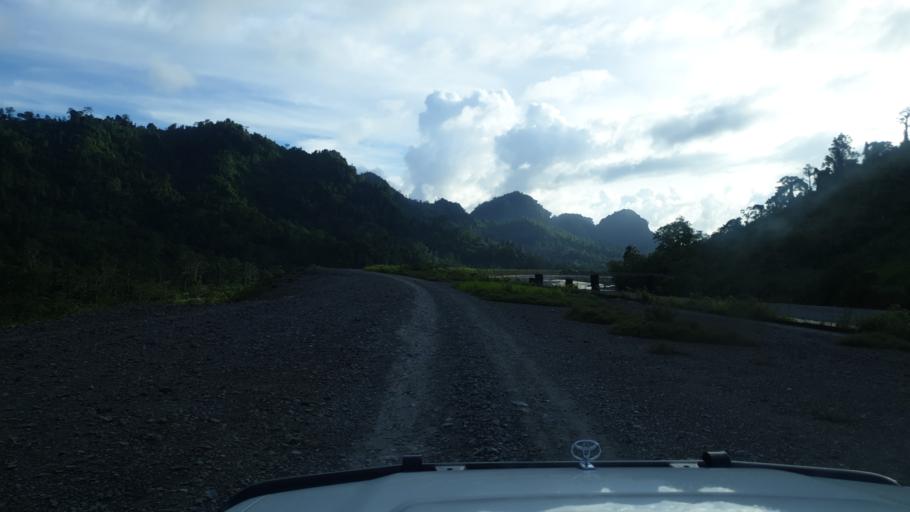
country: PG
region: Bougainville
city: Panguna
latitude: -6.3789
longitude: 155.4323
